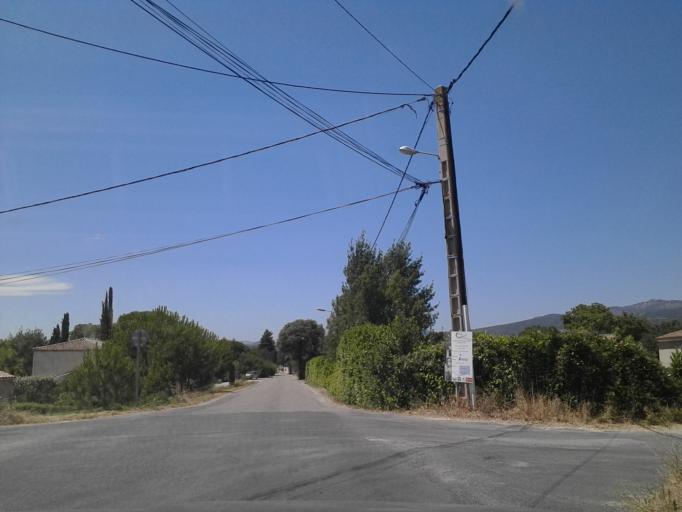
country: FR
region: Languedoc-Roussillon
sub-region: Departement de l'Herault
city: Aniane
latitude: 43.6818
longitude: 3.5849
